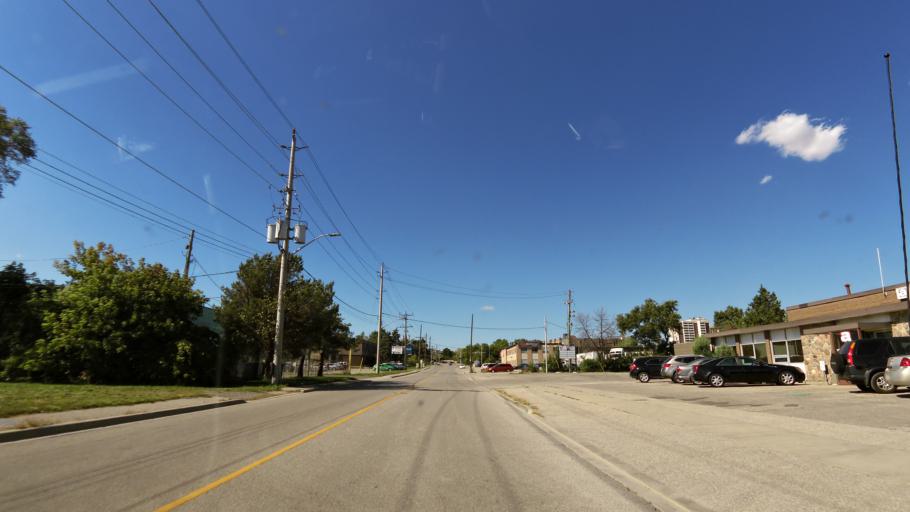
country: CA
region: Ontario
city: Etobicoke
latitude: 43.5951
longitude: -79.5932
